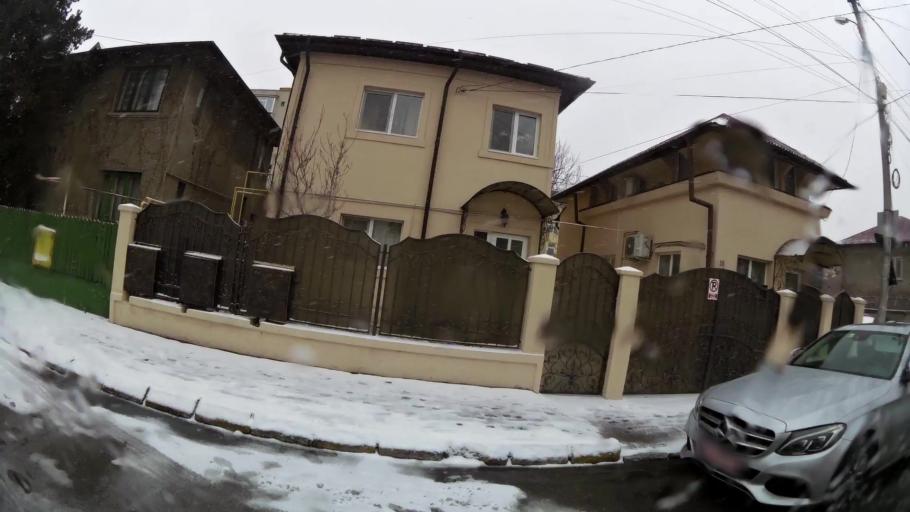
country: RO
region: Dambovita
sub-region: Municipiul Targoviste
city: Targoviste
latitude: 44.9285
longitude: 25.4492
